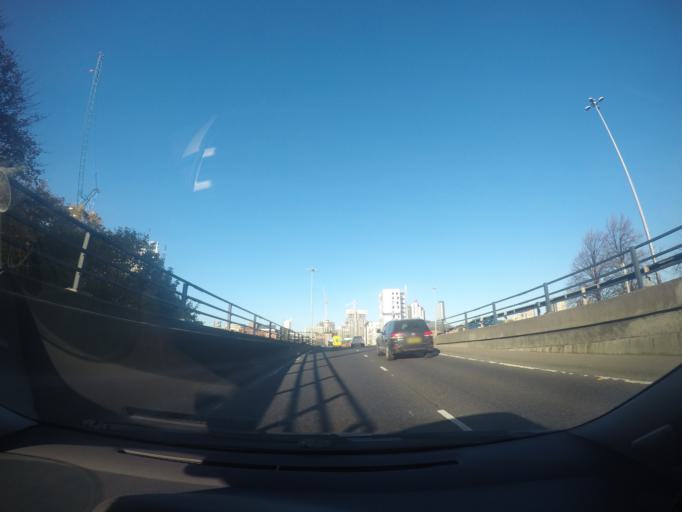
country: GB
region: England
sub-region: City and Borough of Leeds
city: Leeds
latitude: 53.7996
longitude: -1.5329
